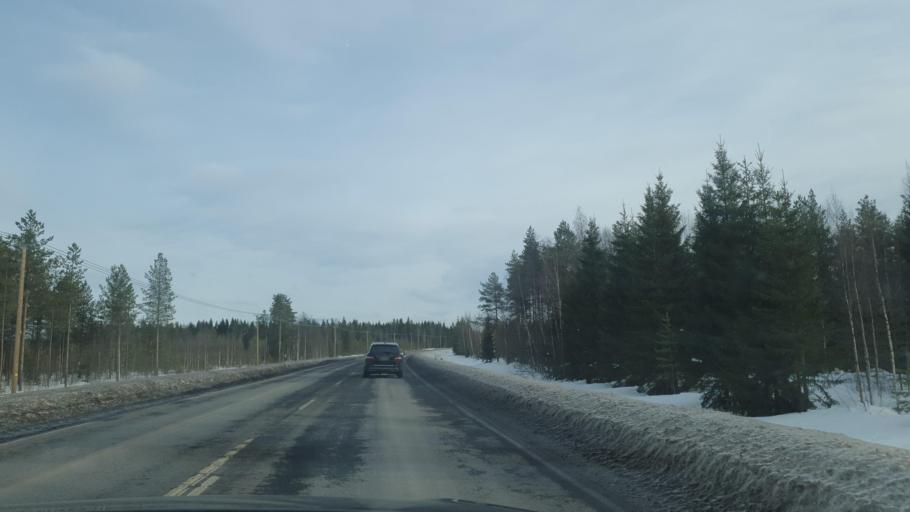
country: FI
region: Northern Ostrobothnia
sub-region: Oulu
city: Muhos
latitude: 64.7874
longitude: 26.1648
